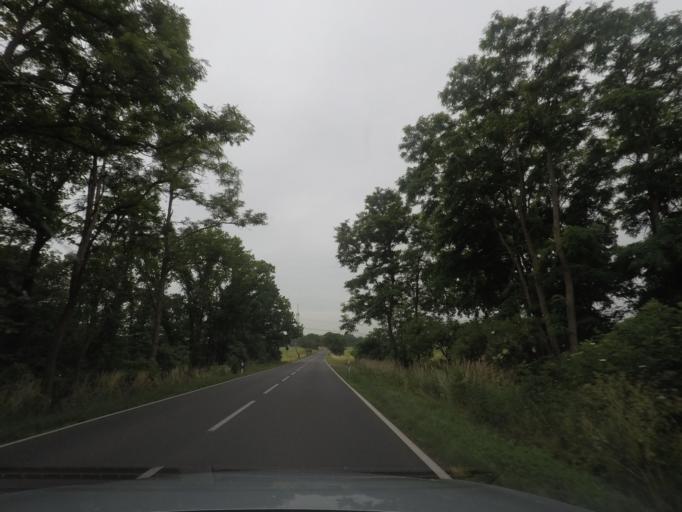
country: DE
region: Saxony-Anhalt
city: Seehausen
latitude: 52.0668
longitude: 11.2855
